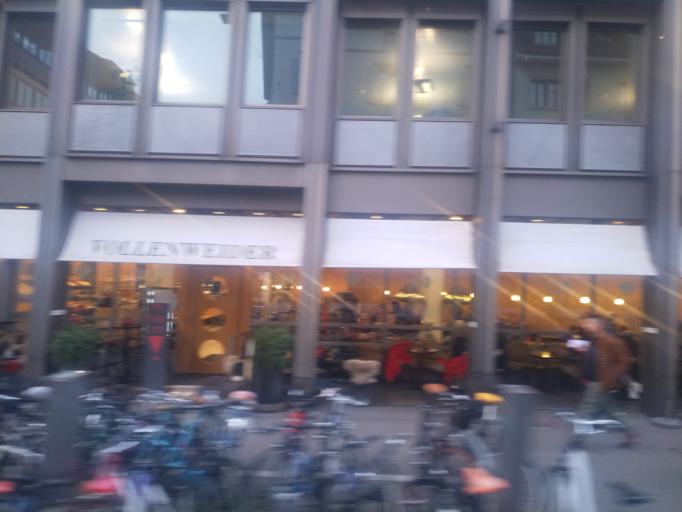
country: CH
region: Zurich
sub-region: Bezirk Winterthur
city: Winterthur
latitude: 47.4998
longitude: 8.7248
